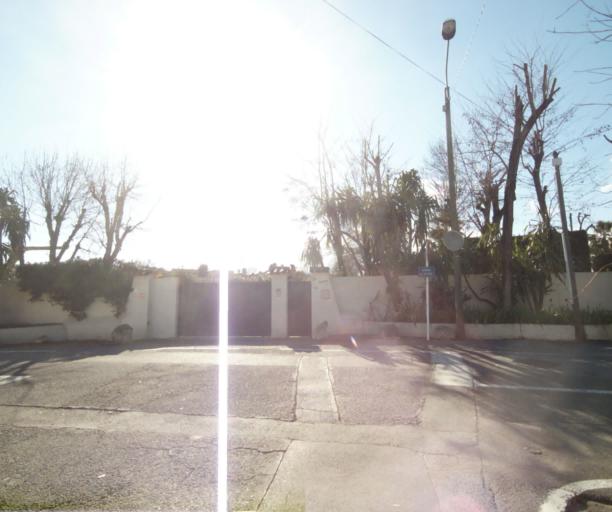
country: FR
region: Provence-Alpes-Cote d'Azur
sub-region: Departement des Alpes-Maritimes
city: Biot
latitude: 43.6136
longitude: 7.1178
